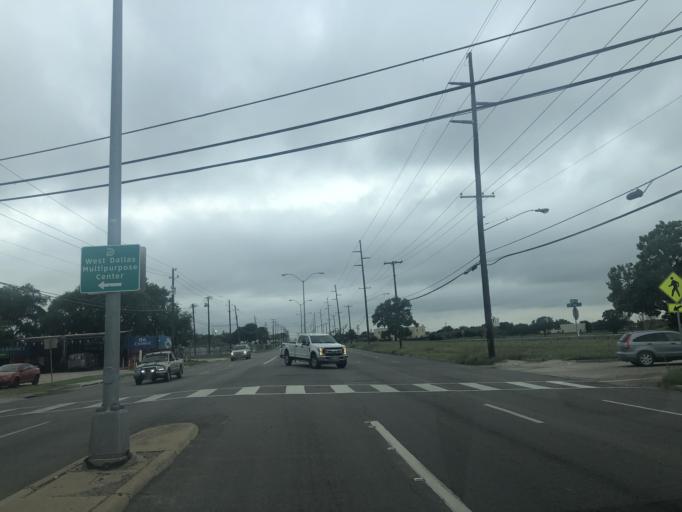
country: US
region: Texas
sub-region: Dallas County
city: Cockrell Hill
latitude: 32.7787
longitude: -96.8605
